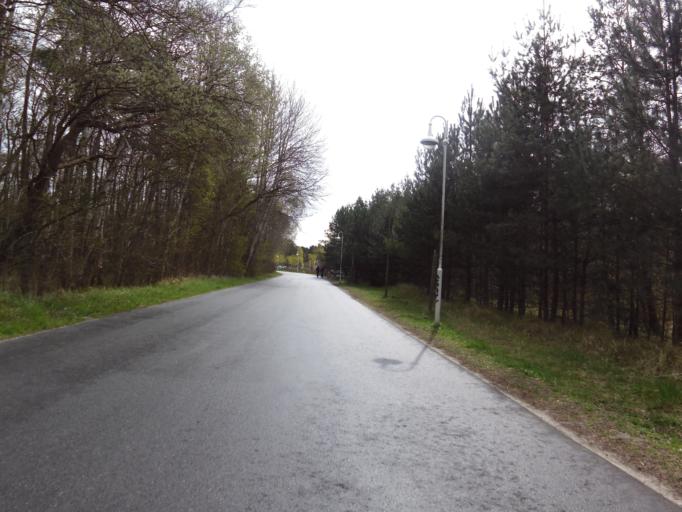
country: DE
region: Mecklenburg-Vorpommern
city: Ostseebad Prerow
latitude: 54.4531
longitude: 12.5515
